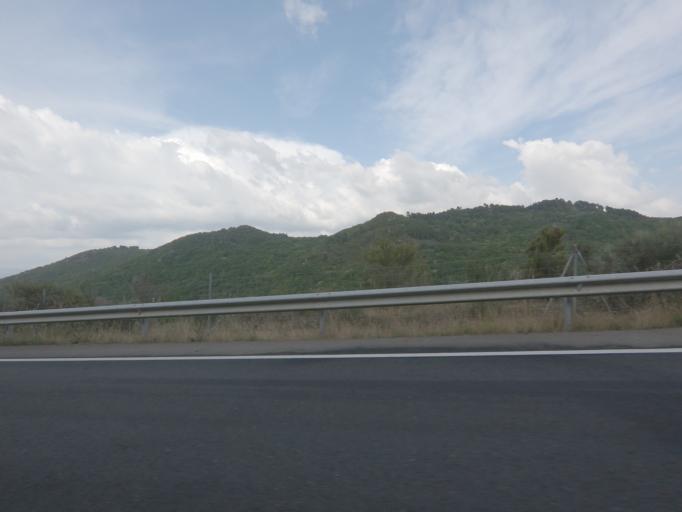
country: ES
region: Galicia
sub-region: Provincia de Ourense
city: Ambia
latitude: 42.1759
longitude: -7.7637
